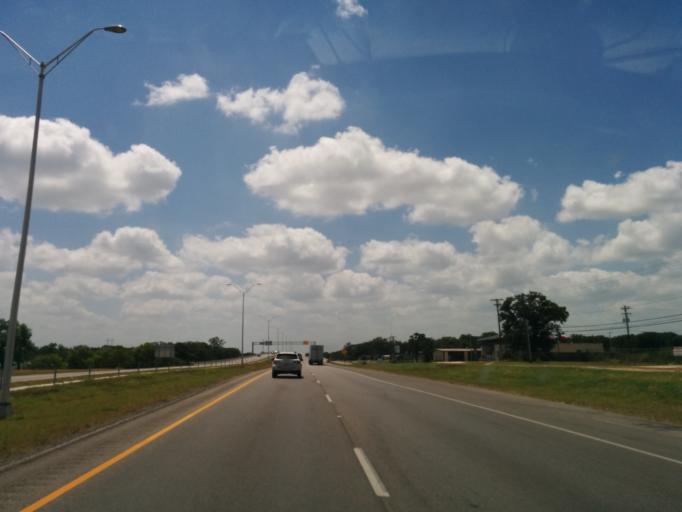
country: US
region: Texas
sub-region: Bastrop County
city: Bastrop
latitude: 30.1112
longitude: -97.3662
